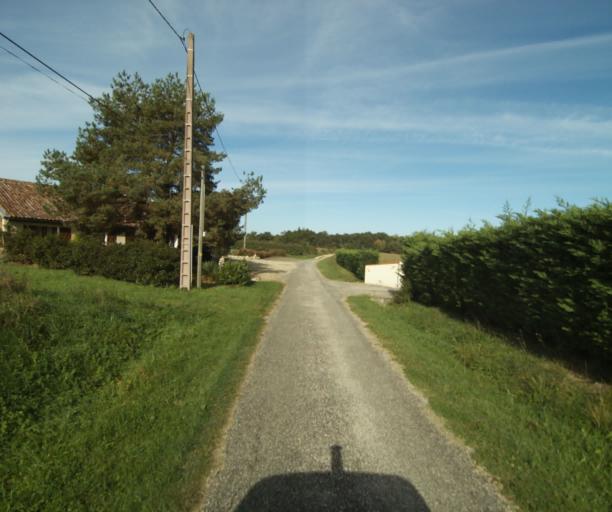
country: FR
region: Midi-Pyrenees
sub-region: Departement du Gers
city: Eauze
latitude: 43.9382
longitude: 0.0907
